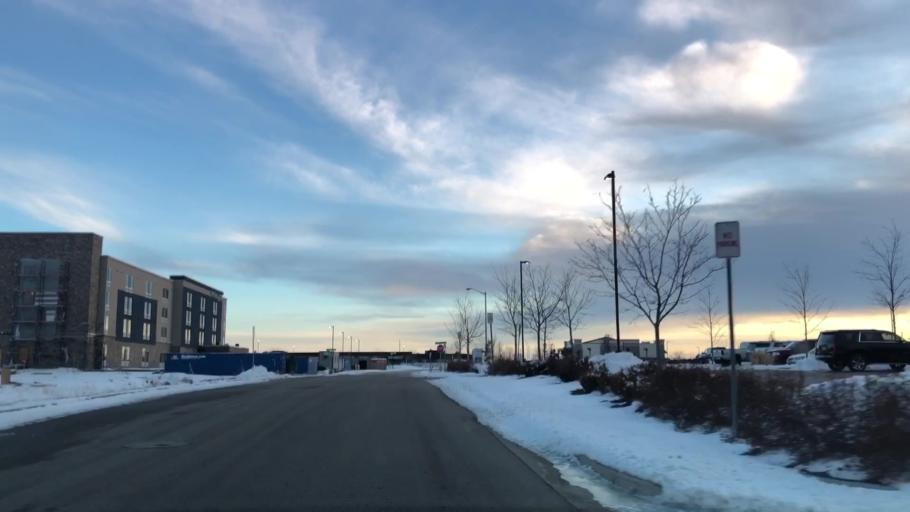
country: US
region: Colorado
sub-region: Weld County
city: Windsor
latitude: 40.4385
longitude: -104.9804
